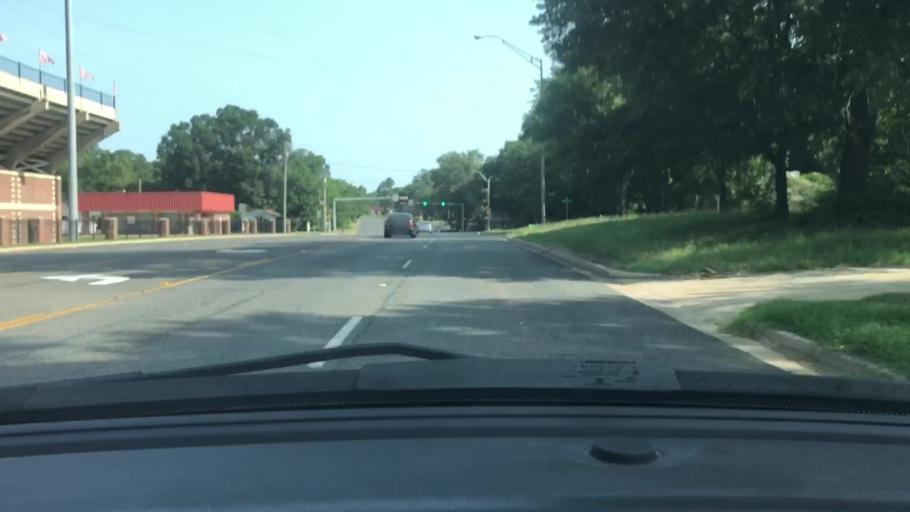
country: US
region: Texas
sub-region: Bowie County
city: Texarkana
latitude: 33.4277
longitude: -94.0614
